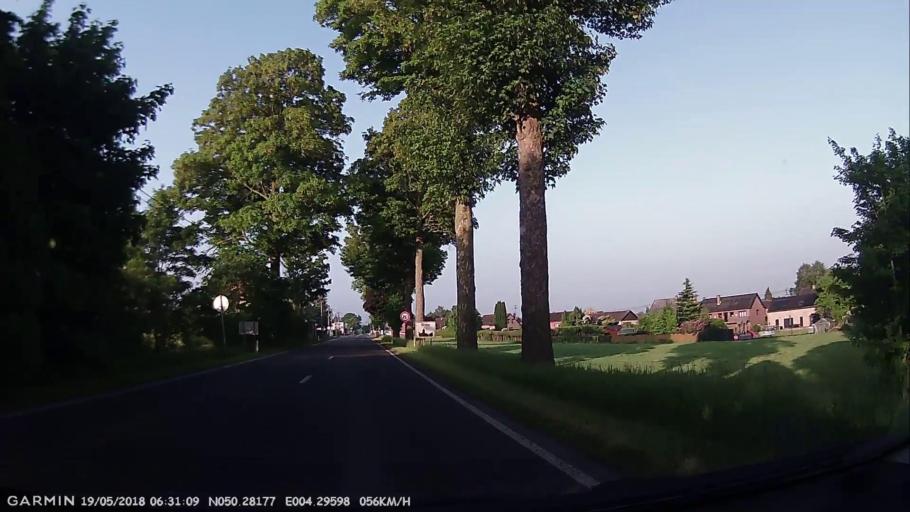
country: BE
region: Wallonia
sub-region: Province du Hainaut
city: Thuin
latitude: 50.2817
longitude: 4.2959
